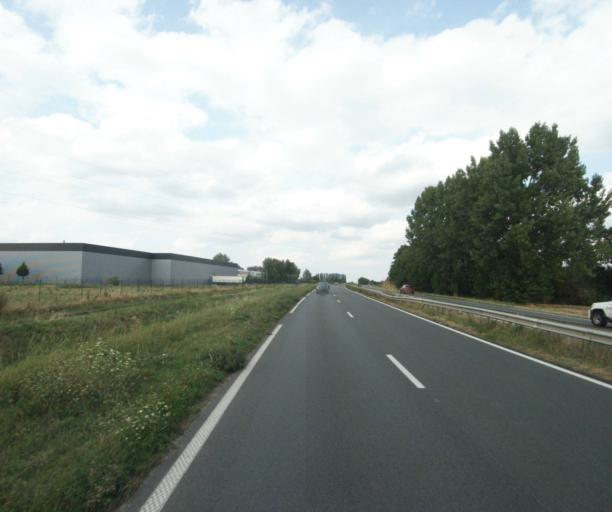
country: FR
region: Nord-Pas-de-Calais
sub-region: Departement du Nord
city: Sailly-lez-Lannoy
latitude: 50.6515
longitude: 3.2069
